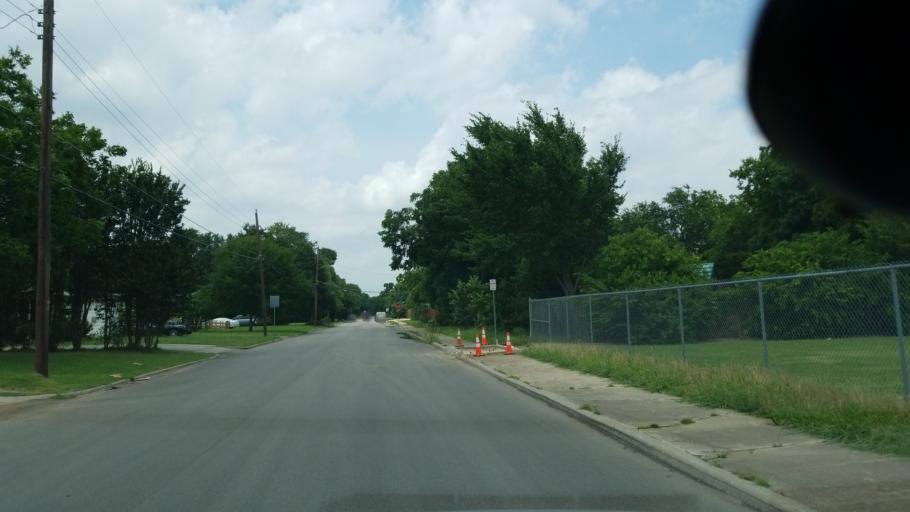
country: US
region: Texas
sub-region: Dallas County
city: Irving
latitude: 32.8245
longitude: -96.9392
